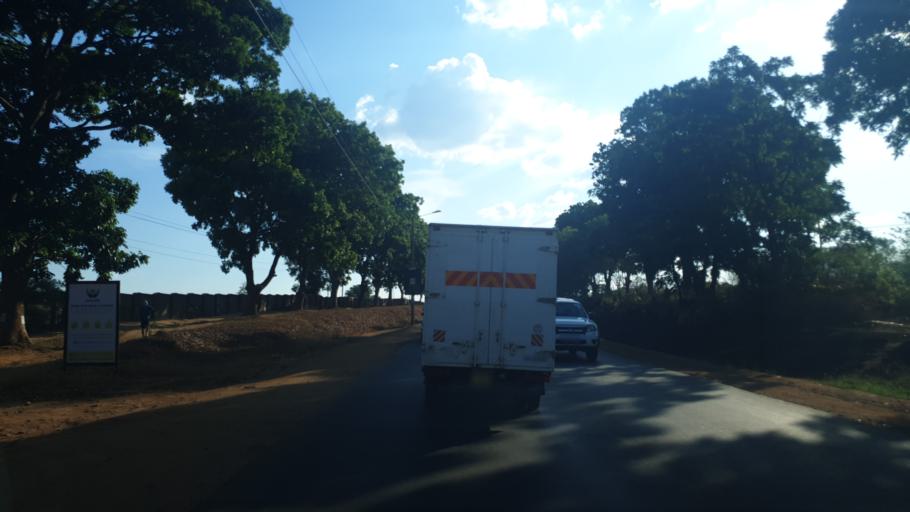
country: MW
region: Central Region
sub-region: Lilongwe District
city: Lilongwe
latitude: -13.9718
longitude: 33.7831
